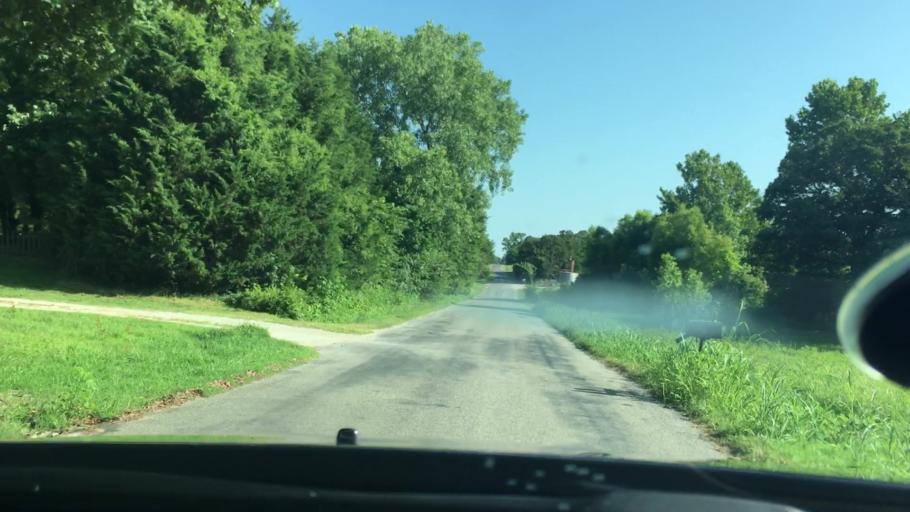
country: US
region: Oklahoma
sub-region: Pontotoc County
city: Byng
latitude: 34.8178
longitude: -96.6258
